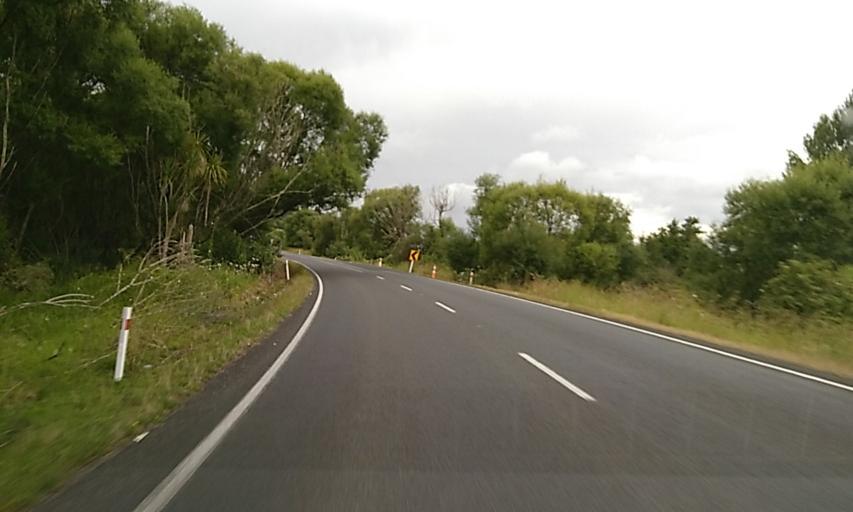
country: NZ
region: Auckland
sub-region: Auckland
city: Pukekohe East
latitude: -37.3039
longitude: 174.9506
